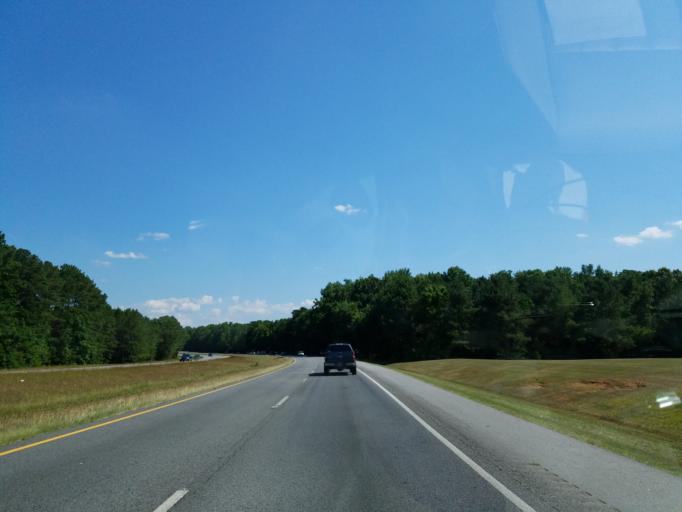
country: US
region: Georgia
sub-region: Spalding County
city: Griffin
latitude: 33.2055
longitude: -84.2890
